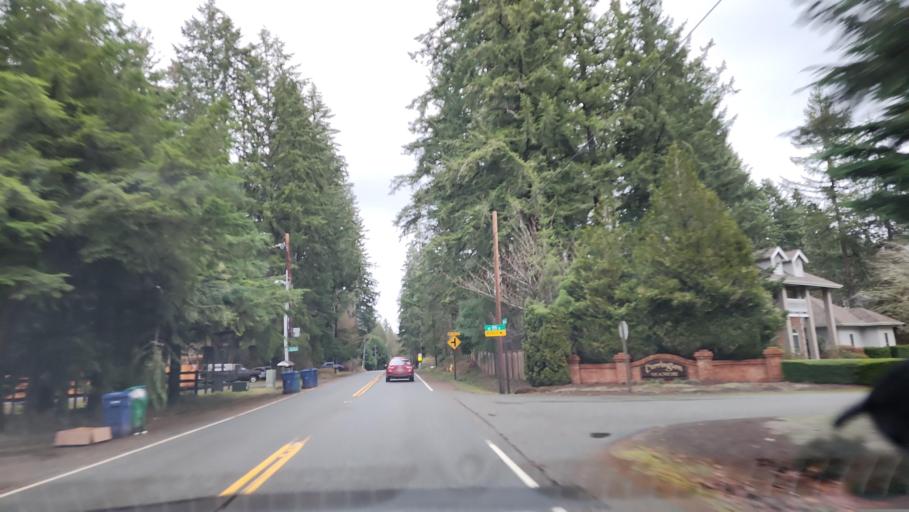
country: US
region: Washington
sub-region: King County
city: Cottage Lake
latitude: 47.7404
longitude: -122.0719
